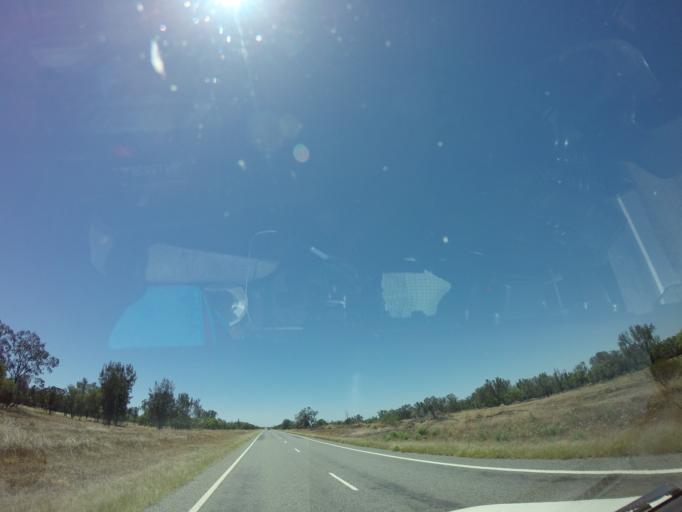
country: AU
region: New South Wales
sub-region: Cobar
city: Cobar
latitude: -31.5811
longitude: 144.8248
